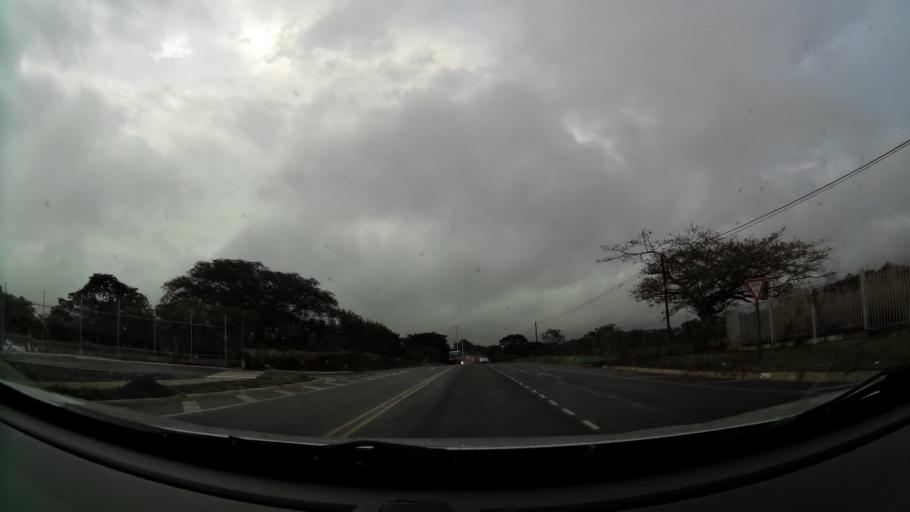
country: CR
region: Alajuela
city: Carrillos
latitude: 9.9759
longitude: -84.2747
